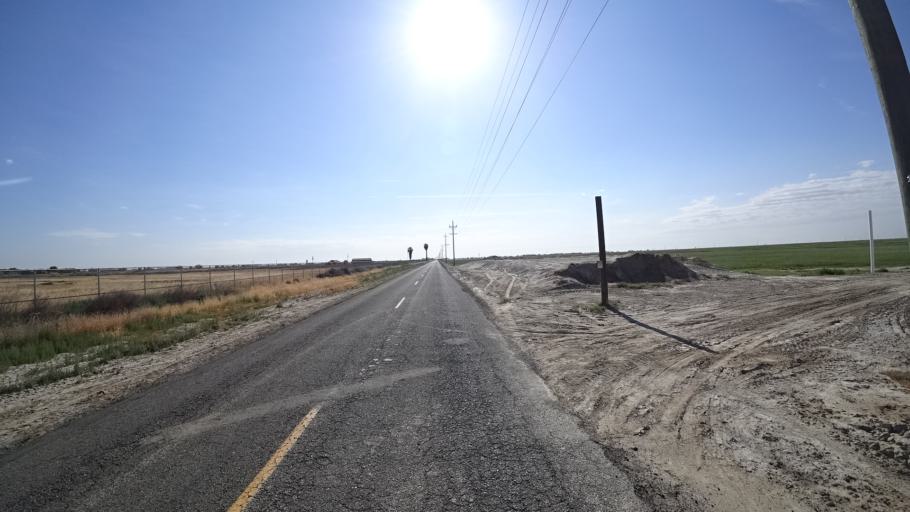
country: US
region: California
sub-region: Kings County
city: Stratford
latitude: 36.2257
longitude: -119.7582
